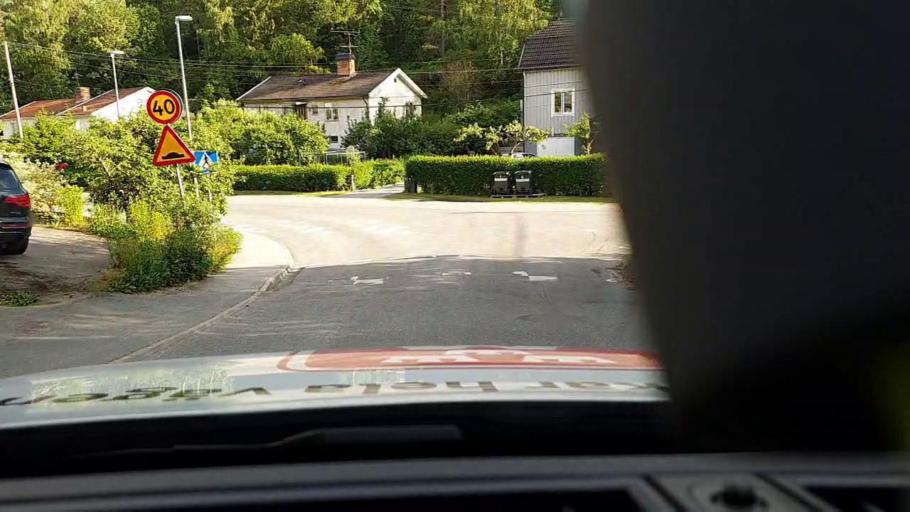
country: SE
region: Stockholm
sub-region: Huddinge Kommun
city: Huddinge
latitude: 59.2607
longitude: 17.9879
